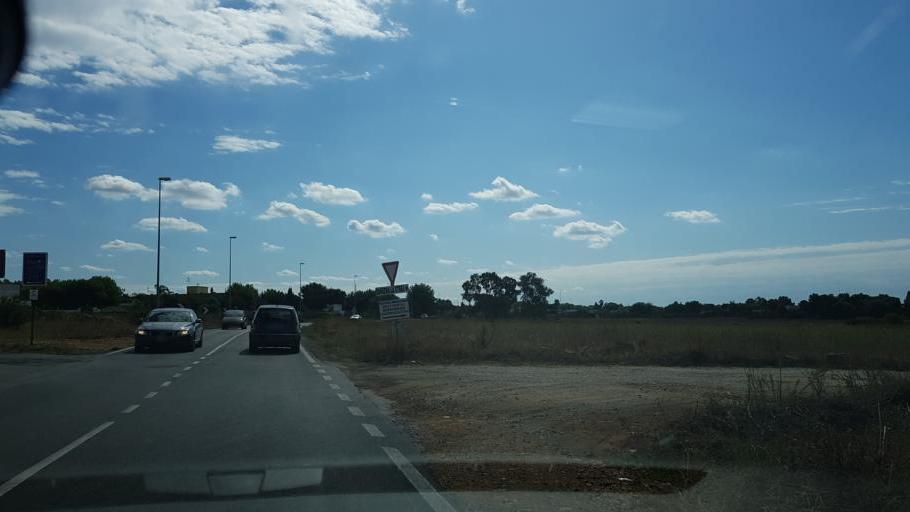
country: IT
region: Apulia
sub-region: Provincia di Lecce
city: Porto Cesareo
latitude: 40.2511
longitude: 17.9101
